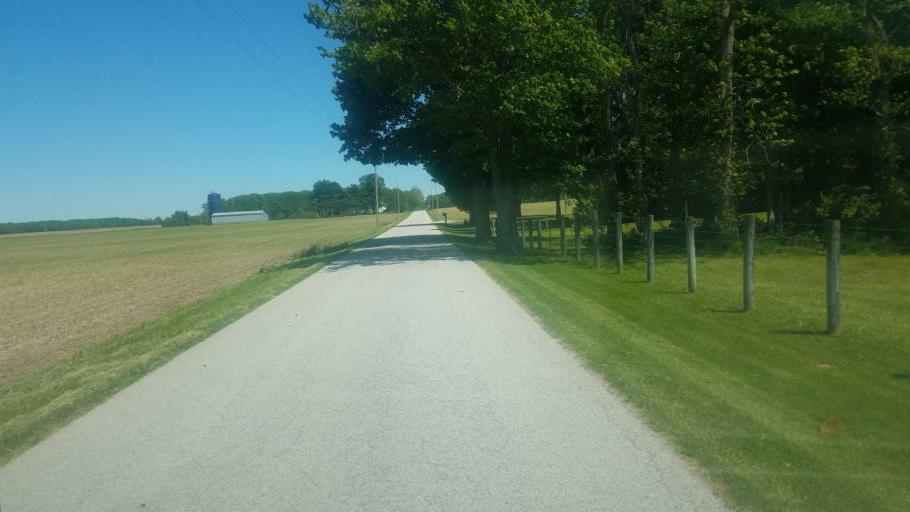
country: US
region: Ohio
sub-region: Champaign County
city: Saint Paris
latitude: 40.1991
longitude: -84.0369
